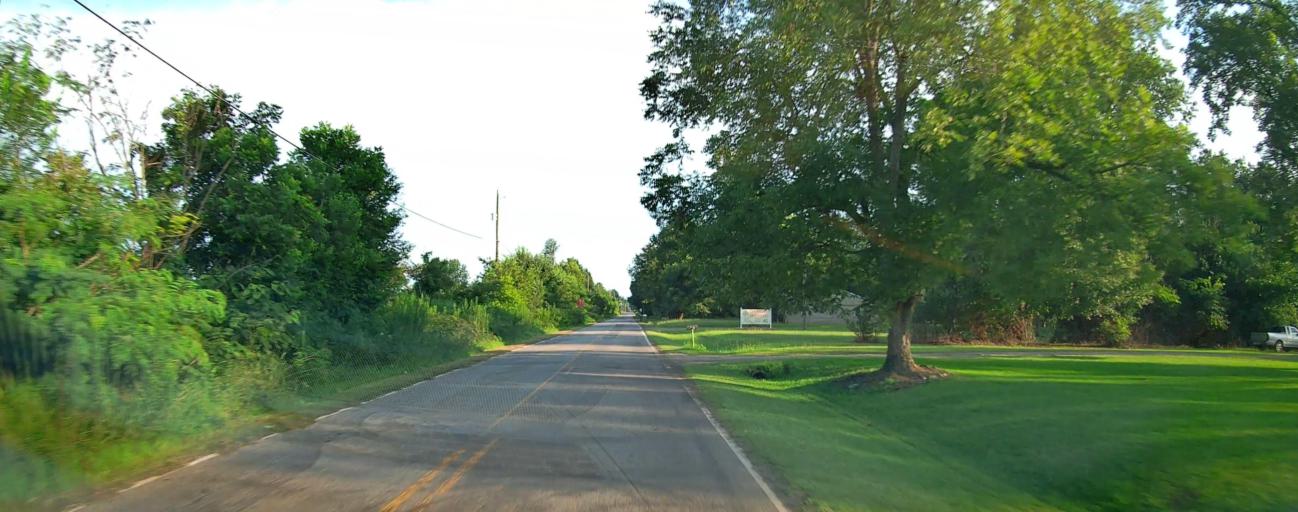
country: US
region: Georgia
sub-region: Peach County
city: Fort Valley
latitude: 32.5771
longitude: -83.8738
